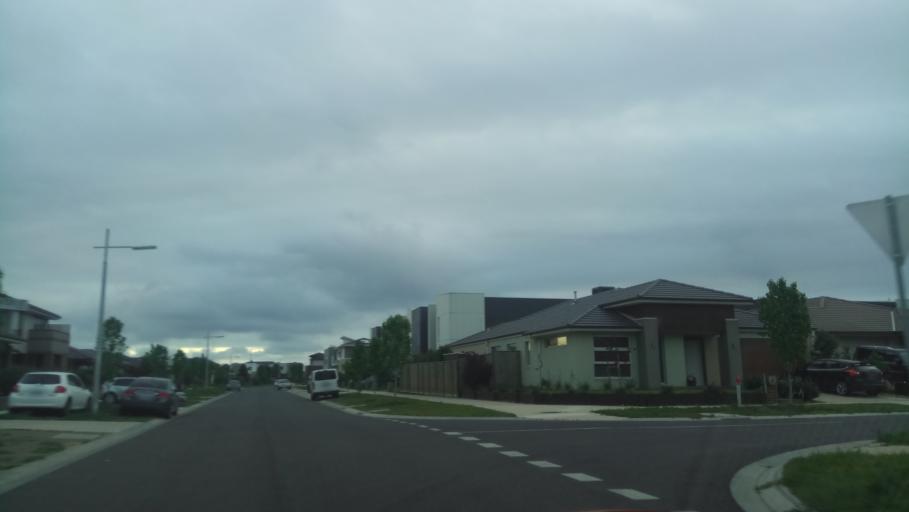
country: AU
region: Victoria
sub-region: Wyndham
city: Point Cook
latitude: -37.9088
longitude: 144.7604
